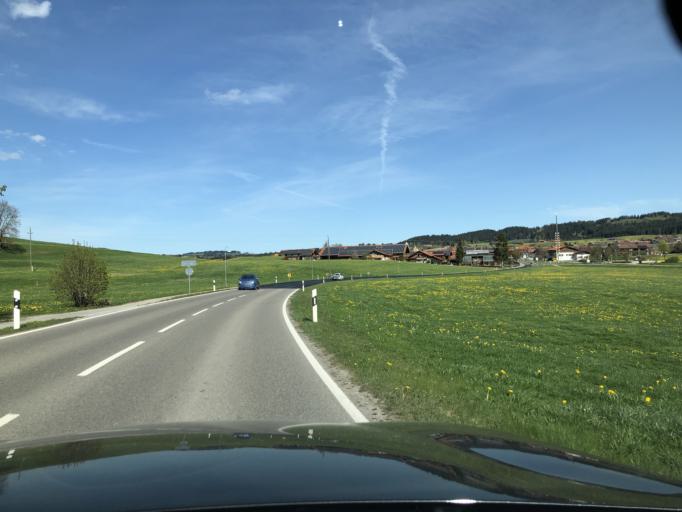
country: DE
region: Bavaria
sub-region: Swabia
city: Hopferau
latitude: 47.6059
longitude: 10.6399
